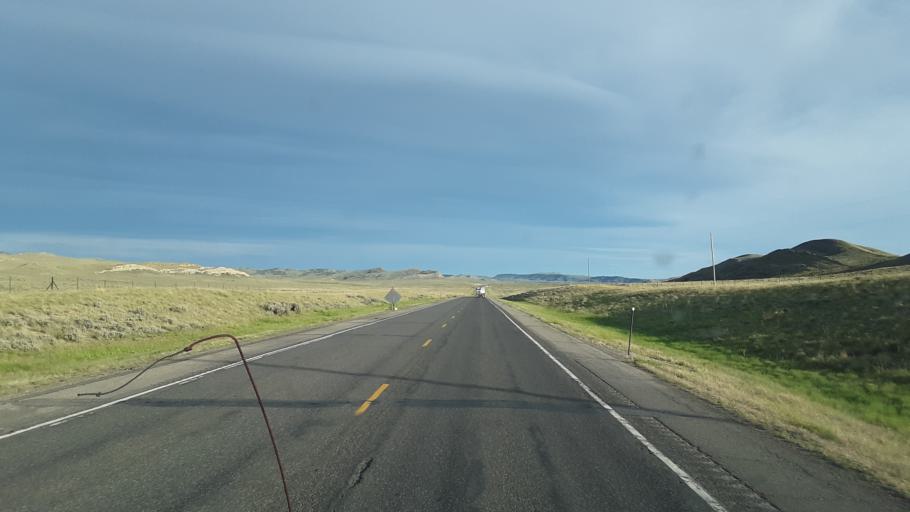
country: US
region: Wyoming
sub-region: Park County
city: Cody
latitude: 44.4856
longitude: -109.0229
